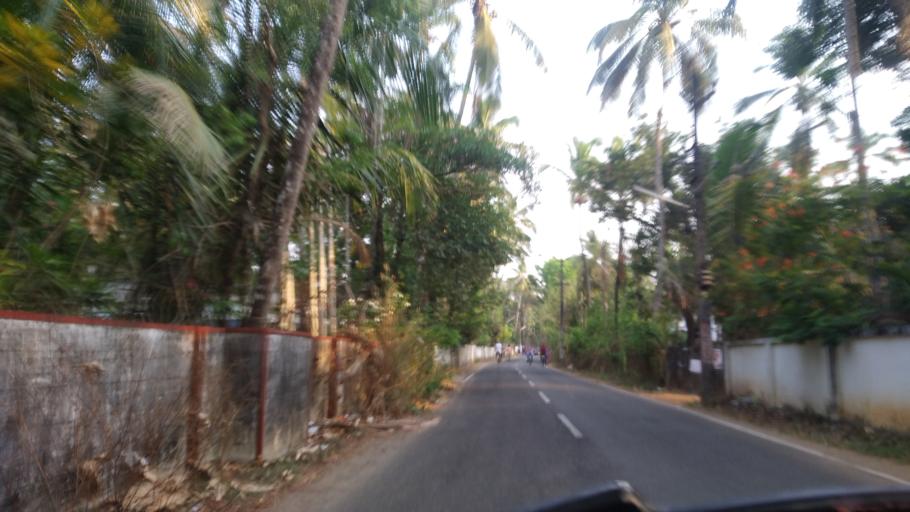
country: IN
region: Kerala
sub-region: Thrissur District
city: Thanniyam
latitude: 10.4085
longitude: 76.0946
